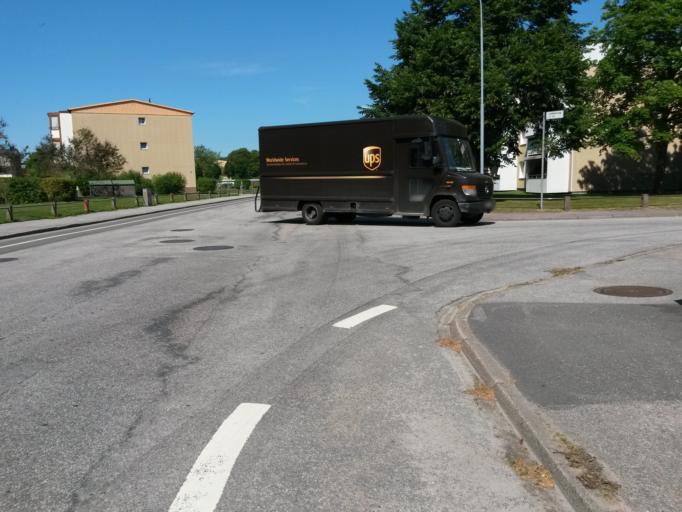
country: SE
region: Vaestra Goetaland
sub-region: Lidkopings Kommun
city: Lidkoping
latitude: 58.4926
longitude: 13.1562
